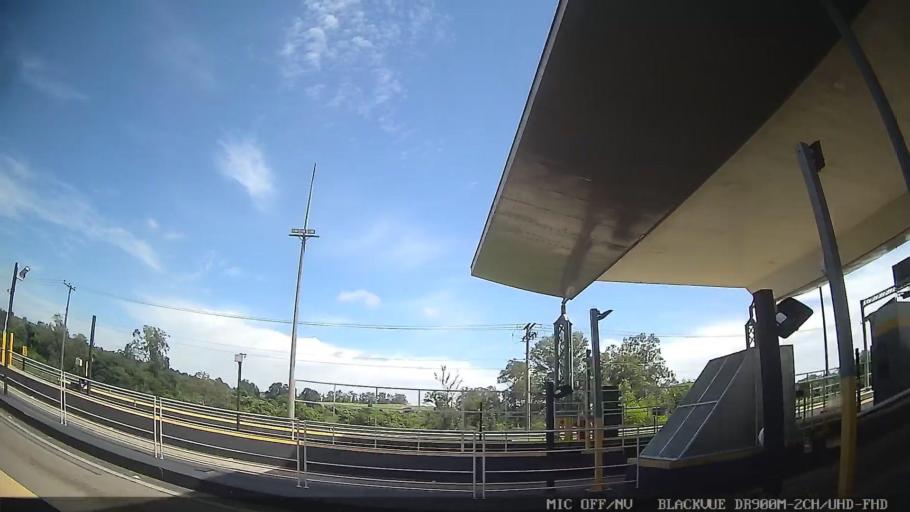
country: BR
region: Sao Paulo
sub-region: Porto Feliz
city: Porto Feliz
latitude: -23.2275
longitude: -47.5628
